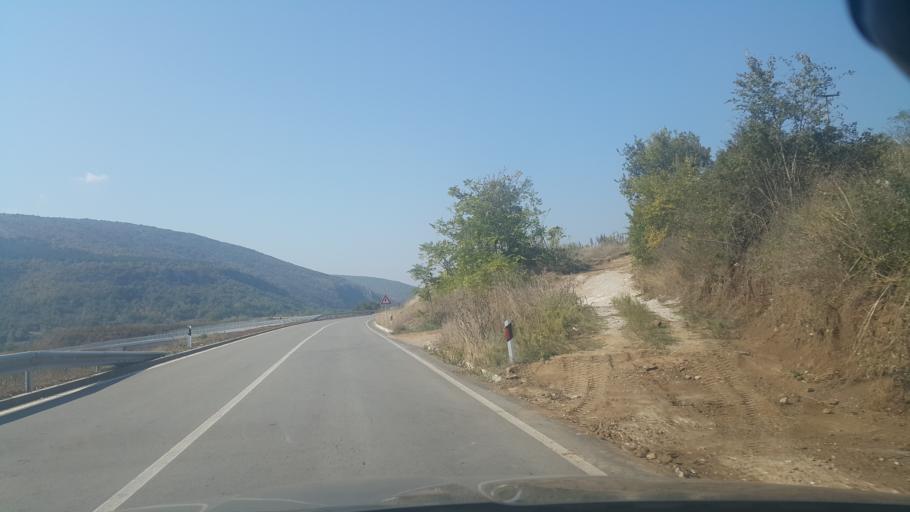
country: RS
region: Central Serbia
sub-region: Pirotski Okrug
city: Pirot
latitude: 43.2146
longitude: 22.5096
